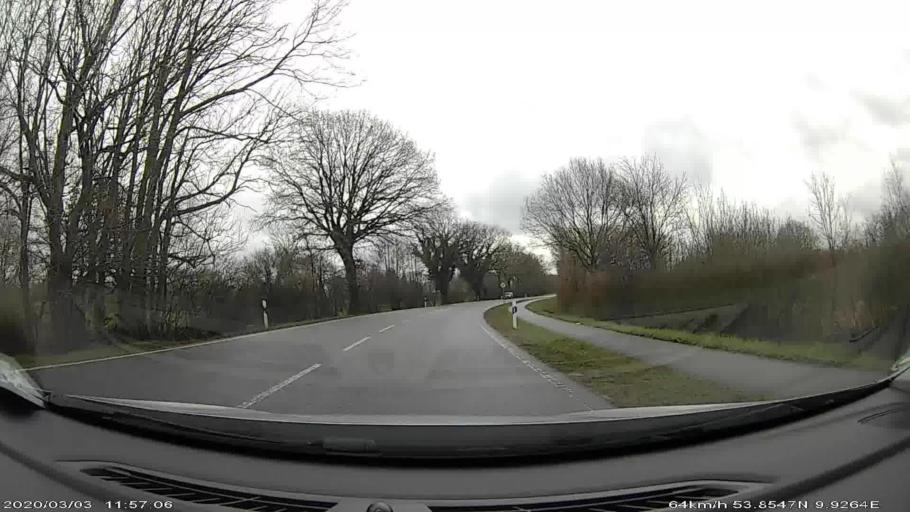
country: DE
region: Schleswig-Holstein
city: Nutzen
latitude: 53.8531
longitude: 9.9284
